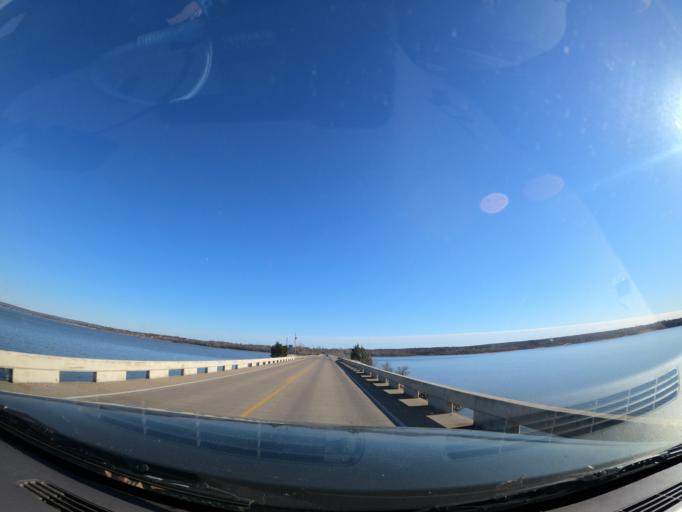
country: US
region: Oklahoma
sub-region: McIntosh County
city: Eufaula
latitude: 35.2451
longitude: -95.5637
